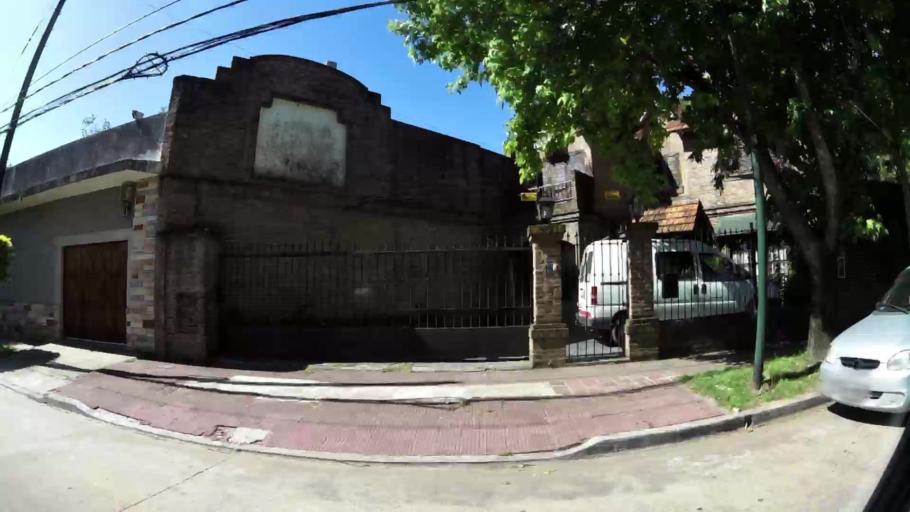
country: AR
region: Buenos Aires
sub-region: Partido de San Isidro
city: San Isidro
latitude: -34.4571
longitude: -58.5329
